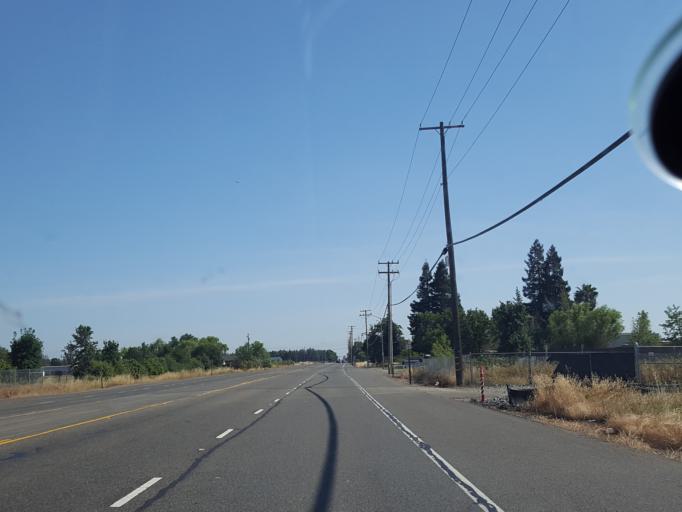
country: US
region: California
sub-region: Sacramento County
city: Rosemont
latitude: 38.5200
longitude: -121.3351
